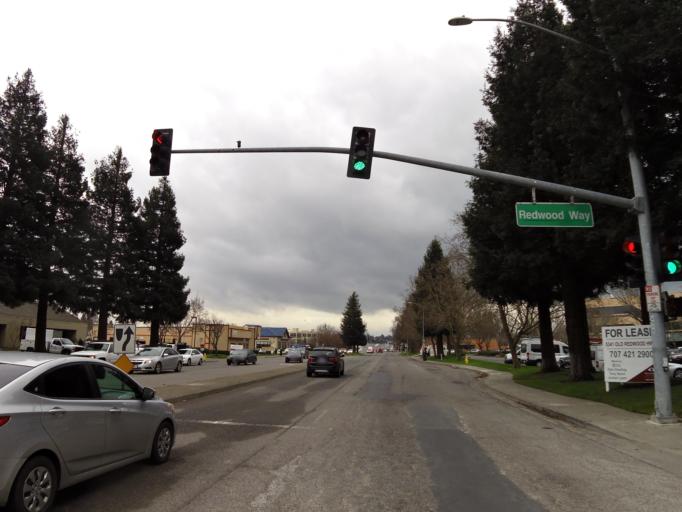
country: US
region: California
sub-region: Sonoma County
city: Penngrove
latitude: 38.2778
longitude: -122.6689
